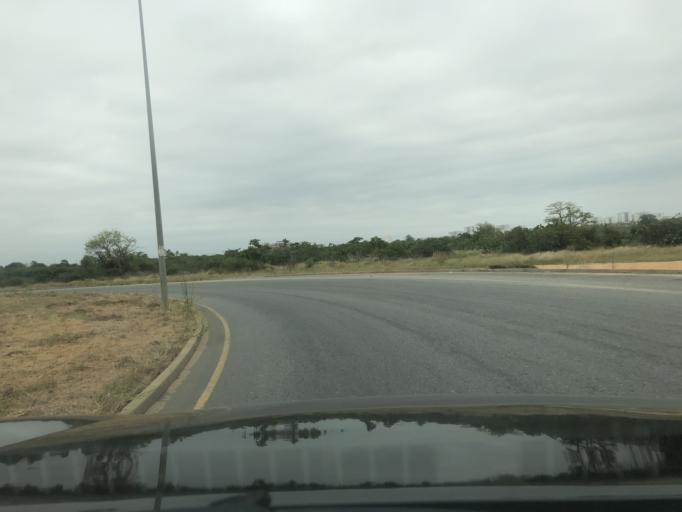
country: AO
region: Luanda
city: Luanda
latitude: -8.9756
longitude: 13.2772
